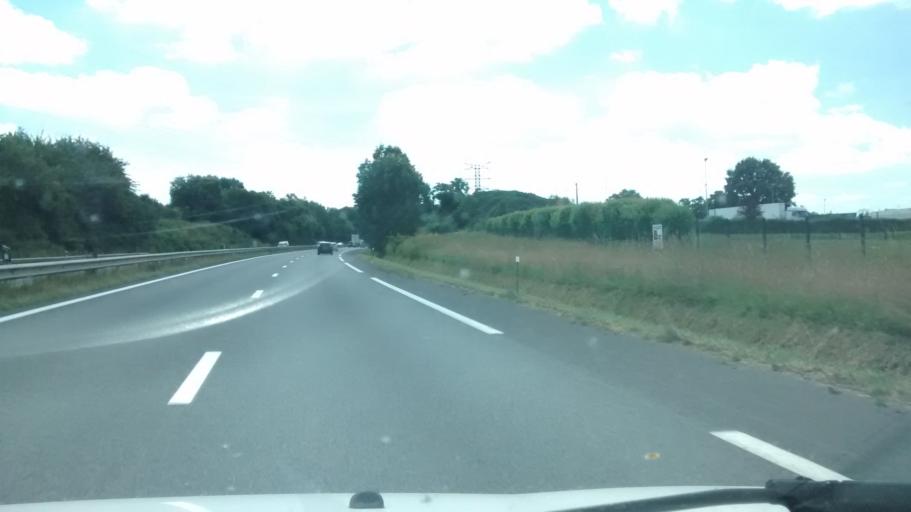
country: FR
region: Brittany
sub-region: Departement d'Ille-et-Vilaine
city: La Chapelle-des-Fougeretz
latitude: 48.1941
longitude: -1.7240
